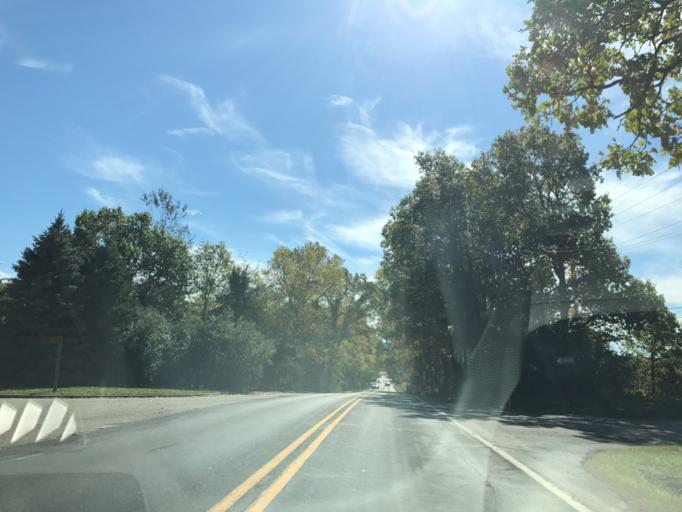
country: US
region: Michigan
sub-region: Washtenaw County
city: Ann Arbor
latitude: 42.2826
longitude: -83.6715
